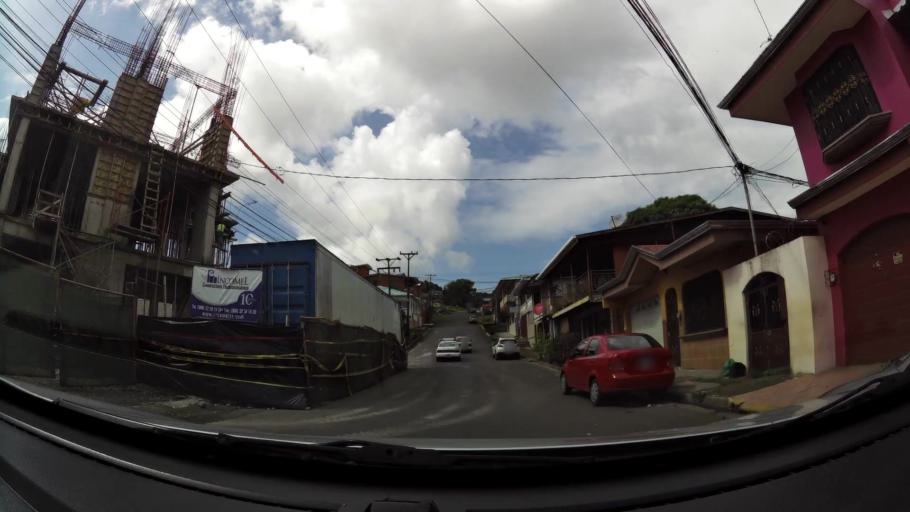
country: CR
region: Limon
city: Limon
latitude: 9.9926
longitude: -83.0335
